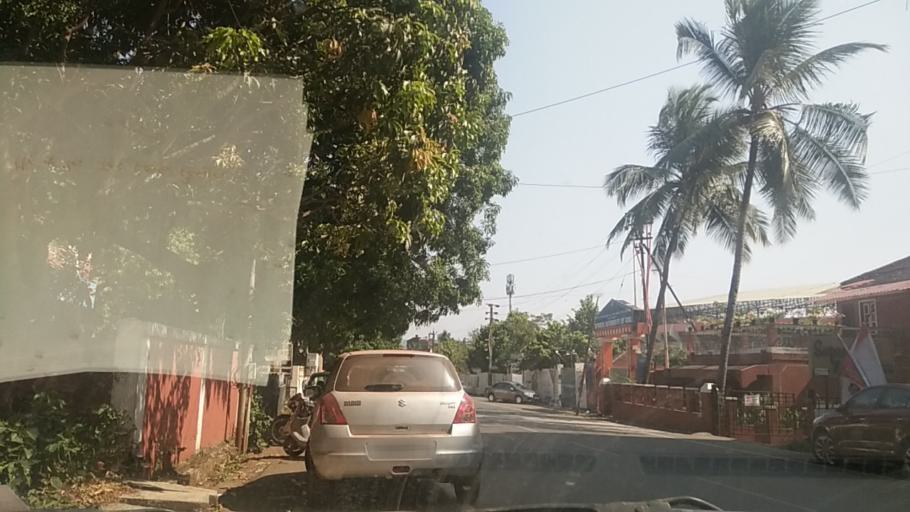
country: IN
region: Goa
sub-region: South Goa
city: Madgaon
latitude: 15.2908
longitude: 73.9611
